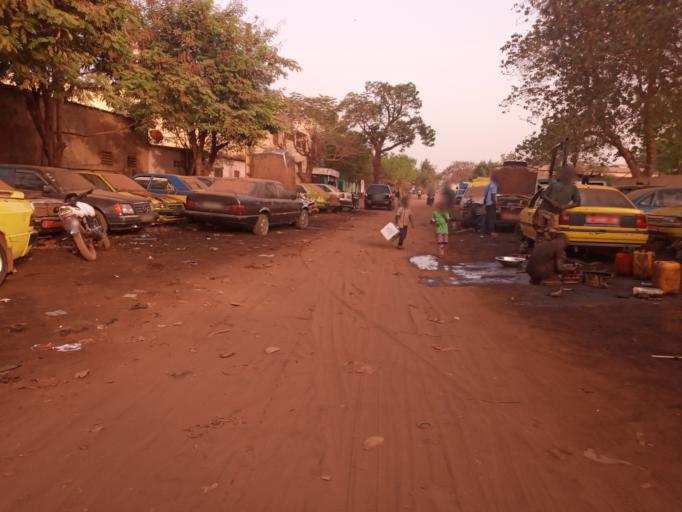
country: ML
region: Bamako
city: Bamako
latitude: 12.5881
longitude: -7.9551
